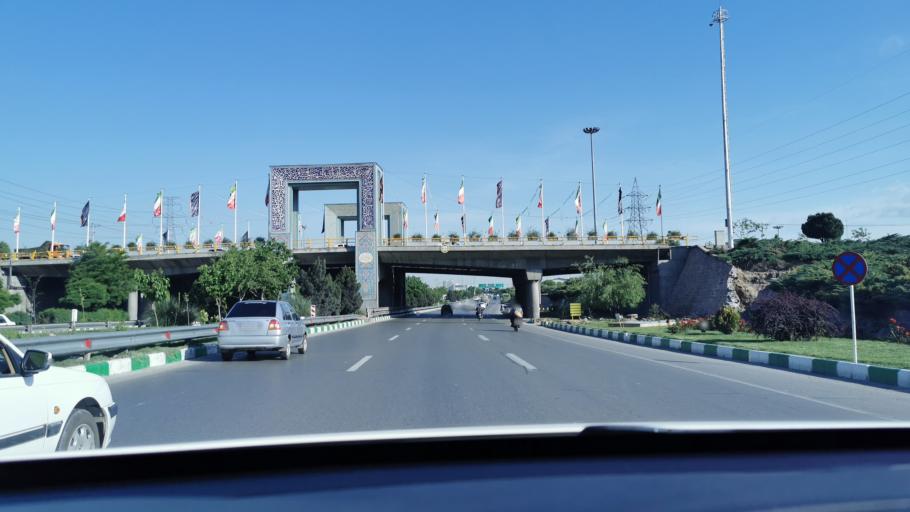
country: IR
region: Razavi Khorasan
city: Mashhad
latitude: 36.2623
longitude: 59.5838
